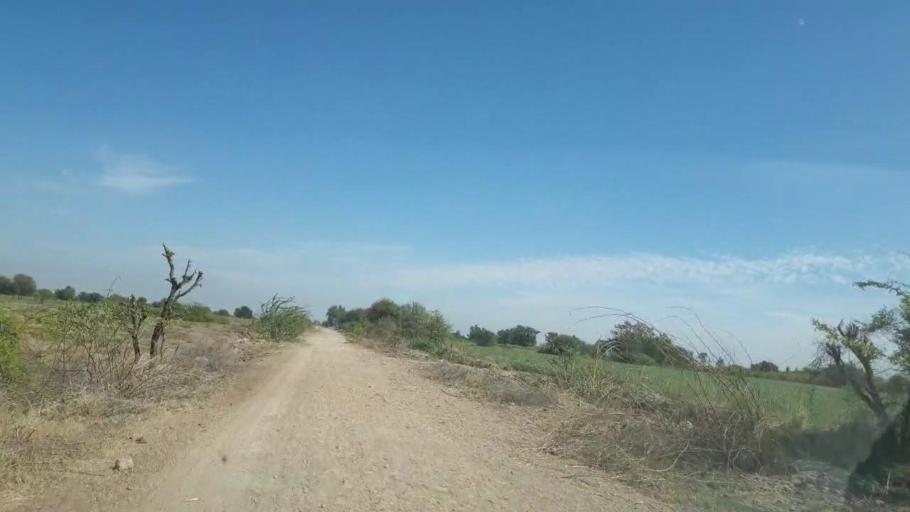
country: PK
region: Sindh
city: Pithoro
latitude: 25.6071
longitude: 69.2759
